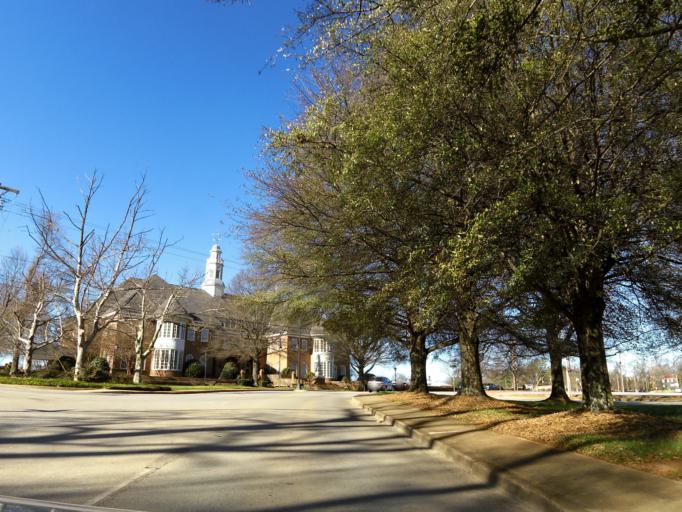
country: US
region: South Carolina
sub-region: Greenville County
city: Greenville
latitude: 34.8509
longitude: -82.4051
